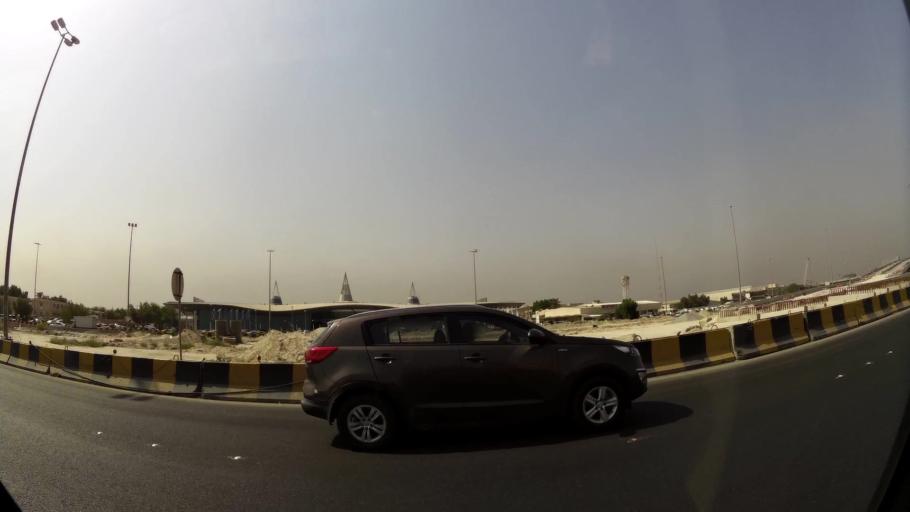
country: KW
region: Al Asimah
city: Ash Shamiyah
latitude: 29.3368
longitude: 47.9500
